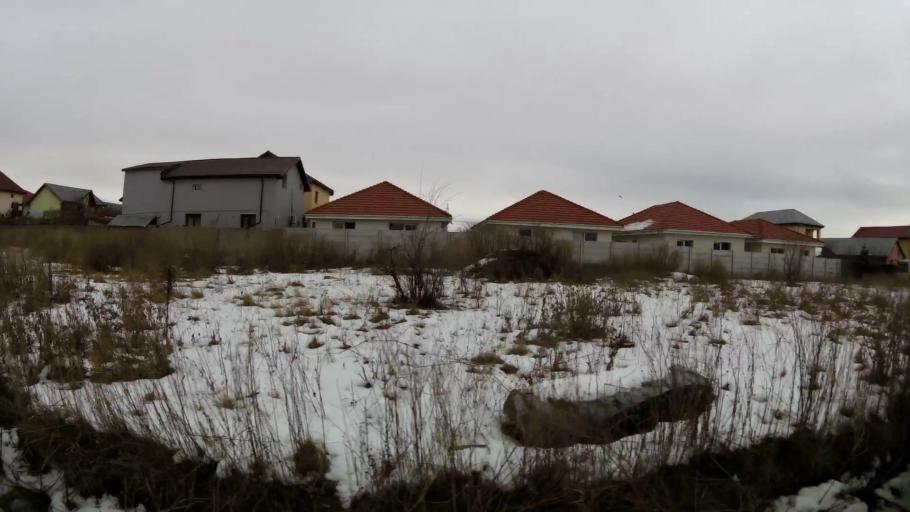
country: RO
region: Ilfov
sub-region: Comuna Pantelimon
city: Pantelimon
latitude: 44.4574
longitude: 26.2163
